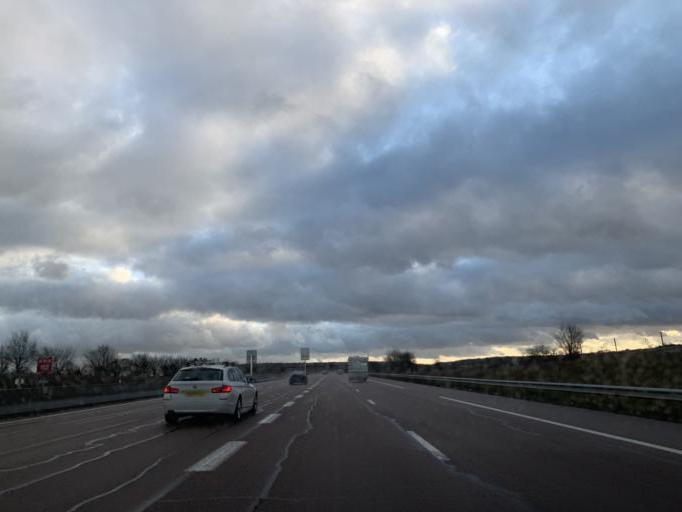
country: FR
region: Champagne-Ardenne
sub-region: Departement de la Haute-Marne
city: Rolampont
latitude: 47.9014
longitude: 5.2235
